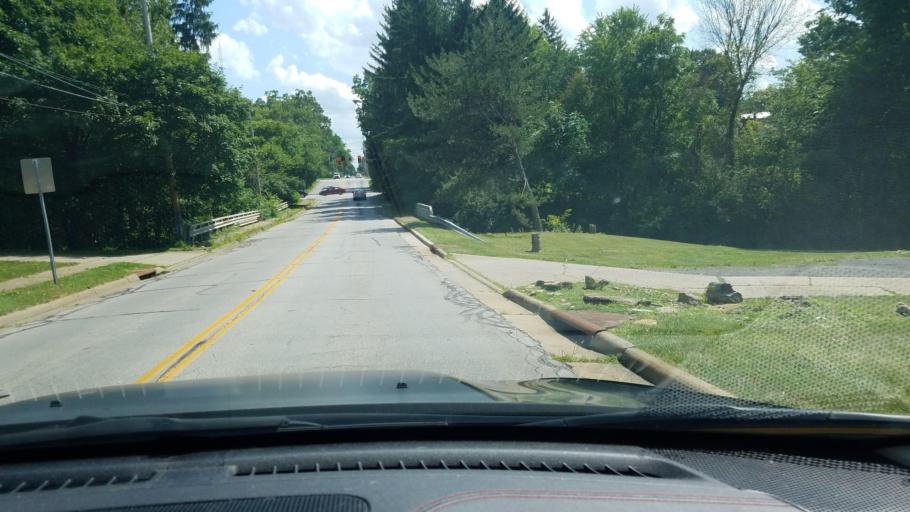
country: US
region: Ohio
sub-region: Mahoning County
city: Youngstown
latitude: 41.0879
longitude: -80.6999
